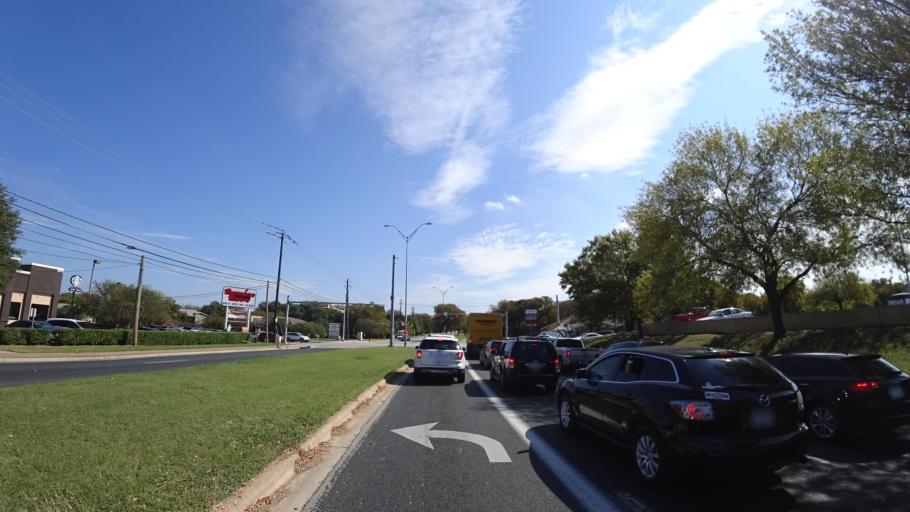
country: US
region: Texas
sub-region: Travis County
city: Shady Hollow
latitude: 30.2074
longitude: -97.8160
